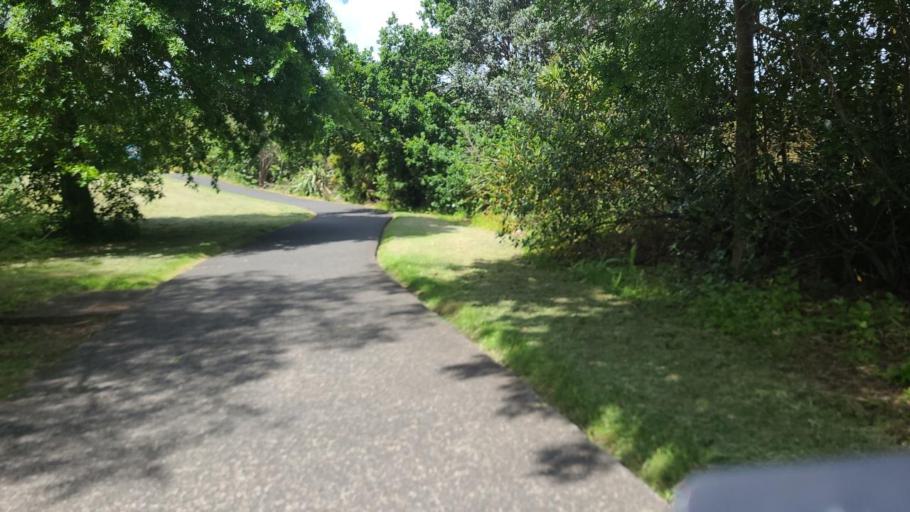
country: NZ
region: Auckland
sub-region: Auckland
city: Rosebank
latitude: -36.8593
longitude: 174.6389
